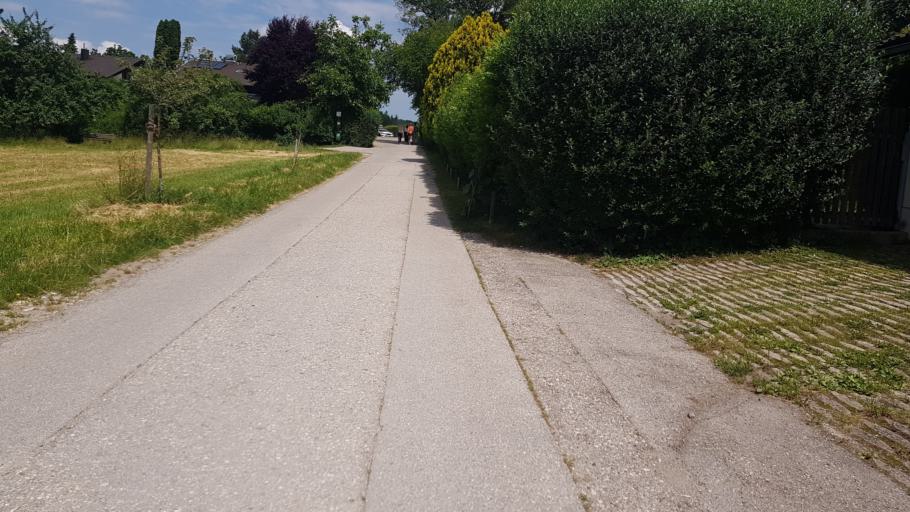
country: DE
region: Bavaria
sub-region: Upper Bavaria
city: Starnberg
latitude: 48.0241
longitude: 11.3714
